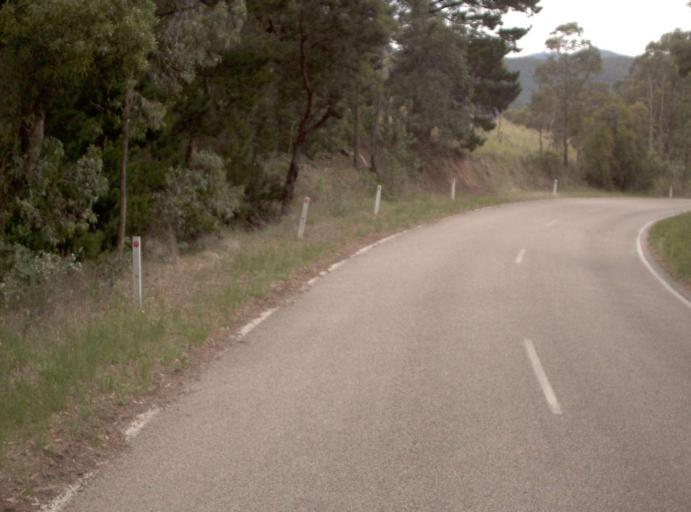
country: AU
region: Victoria
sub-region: East Gippsland
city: Bairnsdale
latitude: -37.5727
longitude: 147.1869
